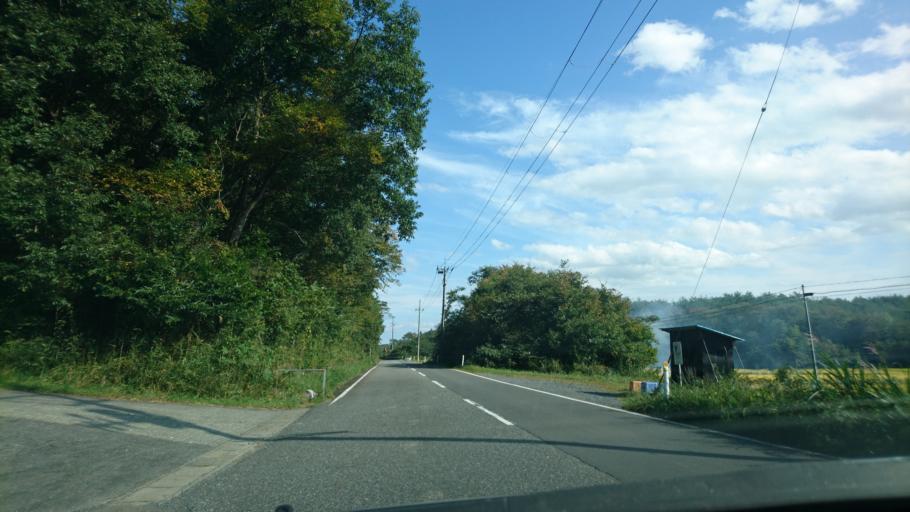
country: JP
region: Iwate
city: Ichinoseki
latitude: 38.8744
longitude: 141.0775
